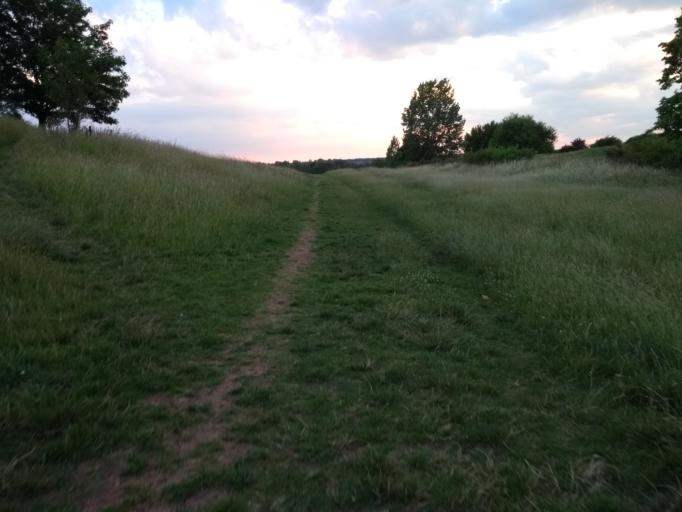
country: GB
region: England
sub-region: Warwickshire
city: Warwick
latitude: 52.2815
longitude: -1.5981
